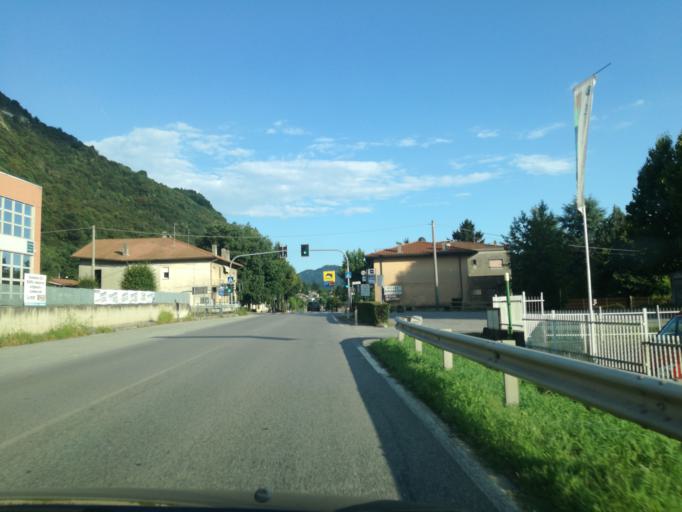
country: IT
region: Lombardy
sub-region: Provincia di Lecco
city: Monte Marenzo
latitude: 45.7625
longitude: 9.4483
